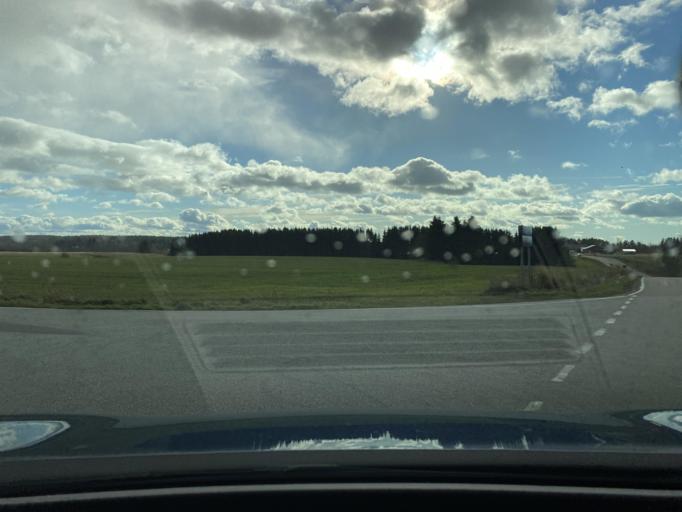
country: FI
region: Varsinais-Suomi
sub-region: Loimaa
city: Aura
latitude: 60.7042
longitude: 22.5921
